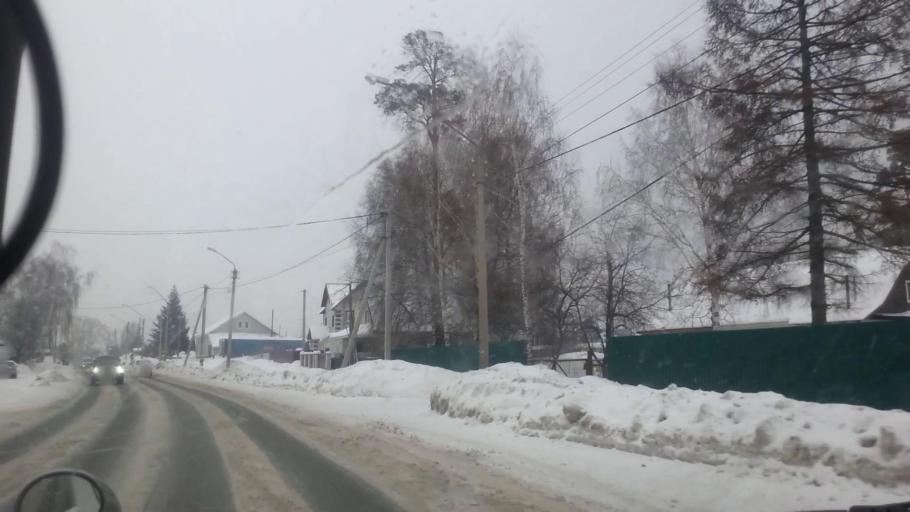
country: RU
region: Altai Krai
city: Vlasikha
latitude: 53.2937
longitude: 83.5736
